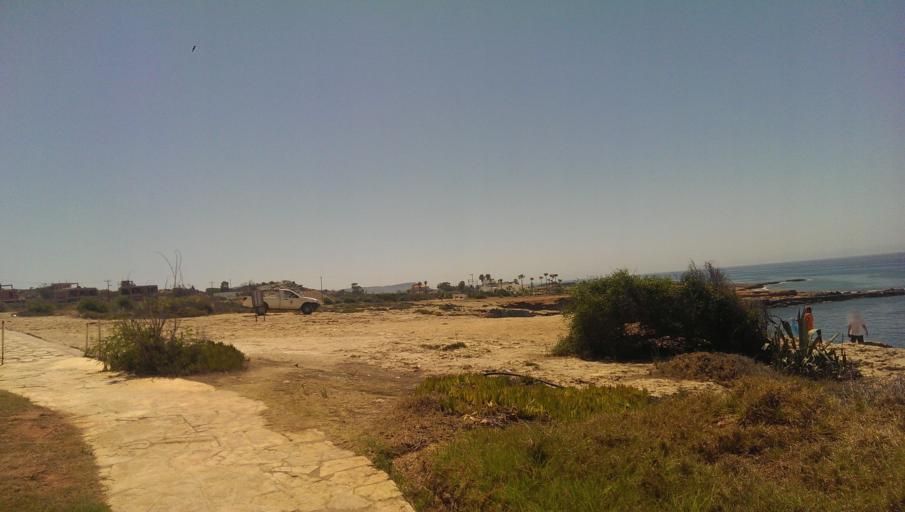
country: CY
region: Ammochostos
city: Ayia Napa
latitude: 34.9830
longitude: 34.0164
